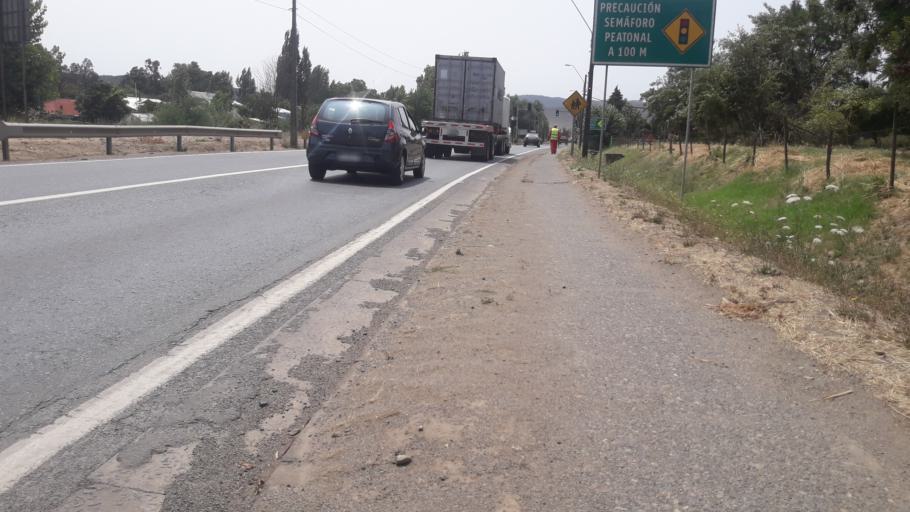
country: CL
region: Biobio
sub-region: Provincia de Biobio
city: Nacimiento
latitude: -37.5047
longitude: -72.6831
